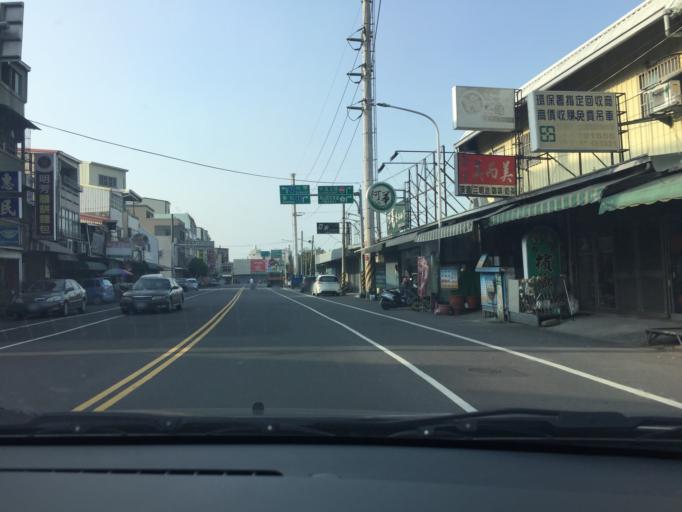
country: TW
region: Taiwan
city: Xinying
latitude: 23.1968
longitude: 120.3181
